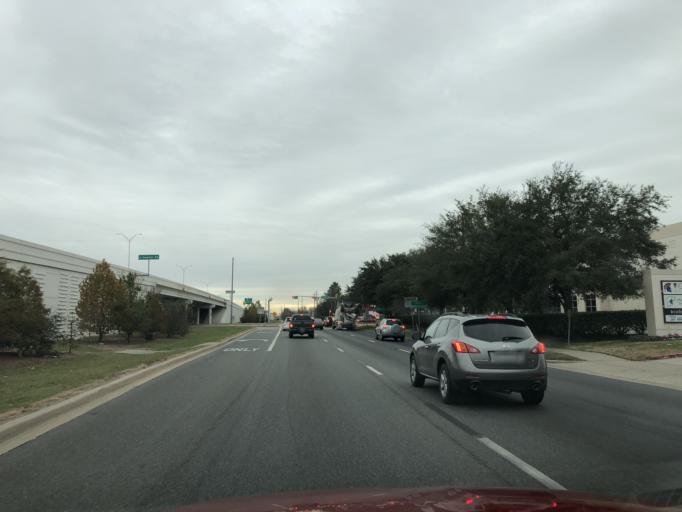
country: US
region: Texas
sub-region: Fort Bend County
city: Missouri City
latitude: 29.6379
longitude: -95.5322
